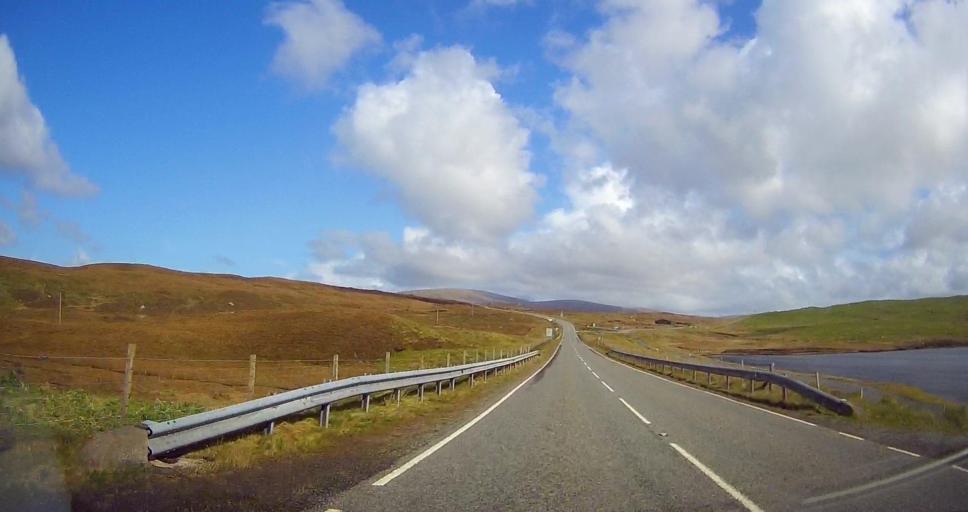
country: GB
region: Scotland
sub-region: Shetland Islands
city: Lerwick
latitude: 60.4724
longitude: -1.4070
